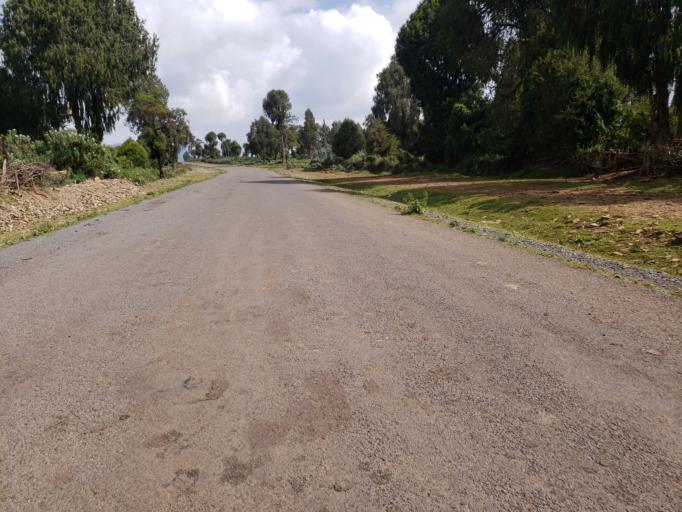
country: ET
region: Oromiya
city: Dodola
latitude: 6.8649
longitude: 39.3910
